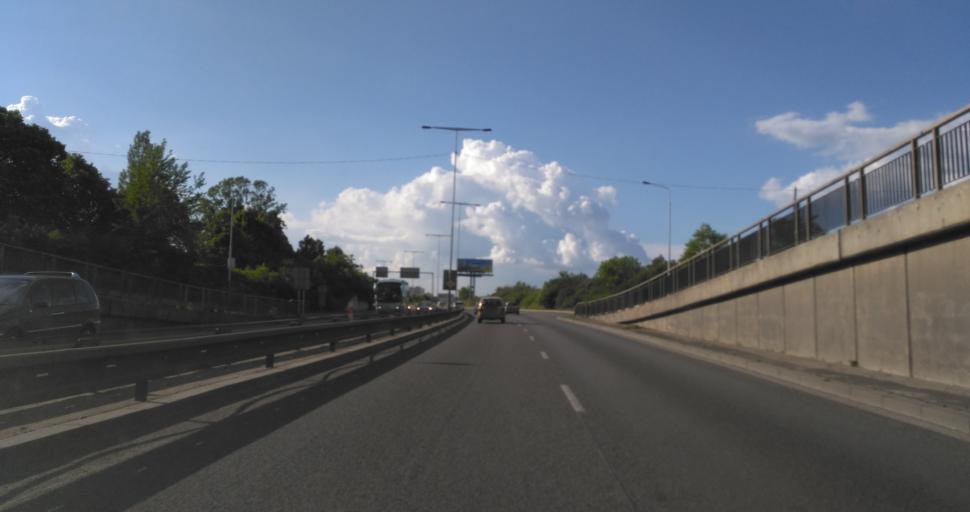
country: CZ
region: Praha
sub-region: Praha 9
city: Vysocany
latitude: 50.1193
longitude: 14.5174
